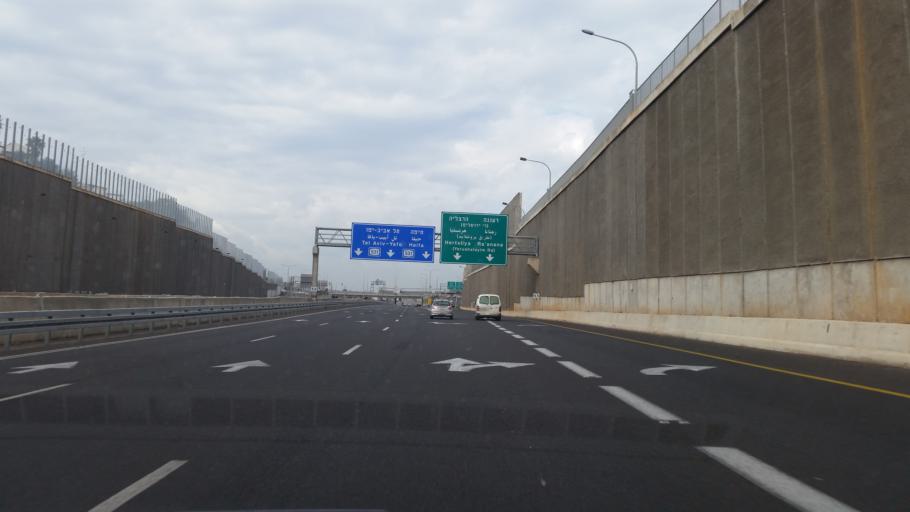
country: IL
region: Central District
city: Ra'anana
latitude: 32.1777
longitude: 34.8575
